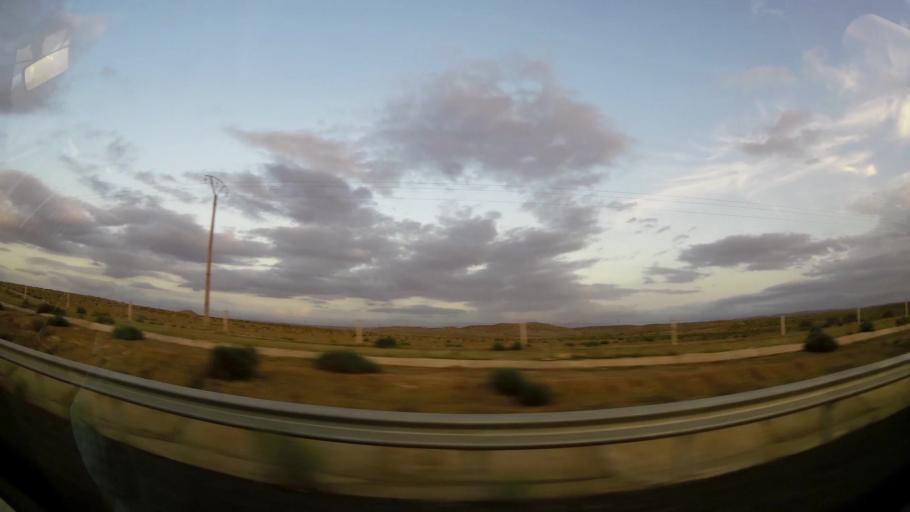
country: MA
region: Oriental
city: Taourirt
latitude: 34.5567
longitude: -2.8431
